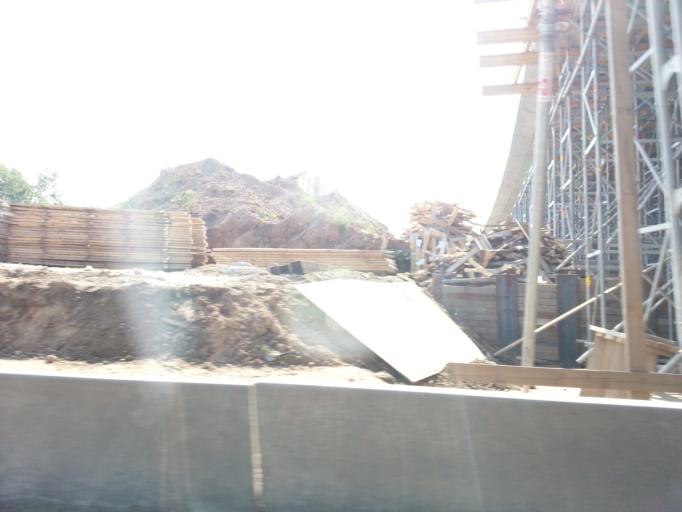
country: LT
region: Vilnius County
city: Pasilaiciai
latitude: 54.7353
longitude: 25.2084
